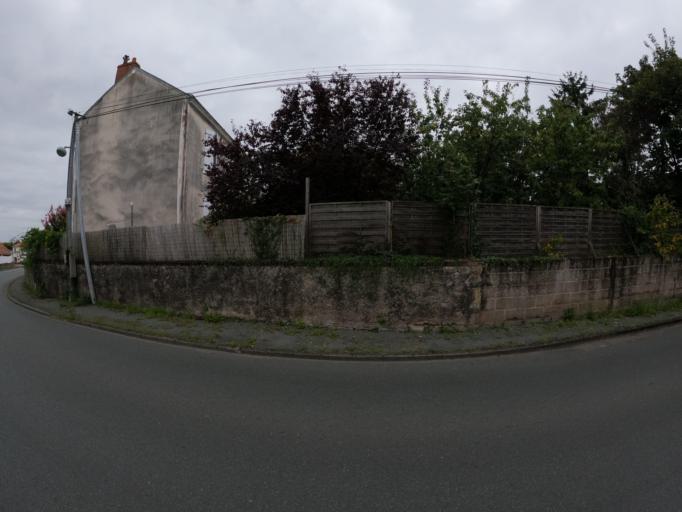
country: FR
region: Pays de la Loire
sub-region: Departement de la Vendee
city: Saint-Martin-sous-Mouzeuil
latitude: 46.5083
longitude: -0.9504
